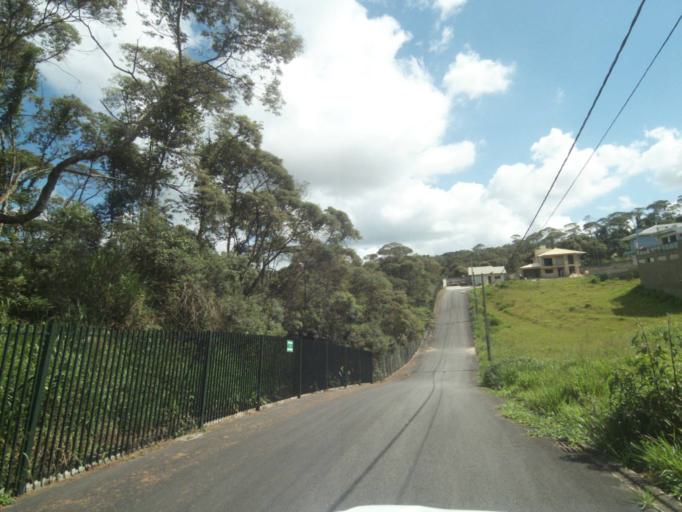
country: BR
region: Parana
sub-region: Colombo
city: Colombo
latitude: -25.3098
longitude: -49.2347
